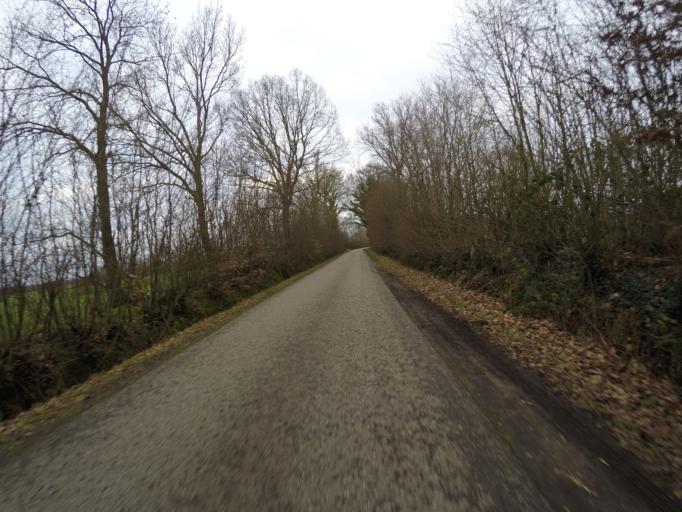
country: DE
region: Schleswig-Holstein
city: Alveslohe
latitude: 53.7976
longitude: 9.9028
